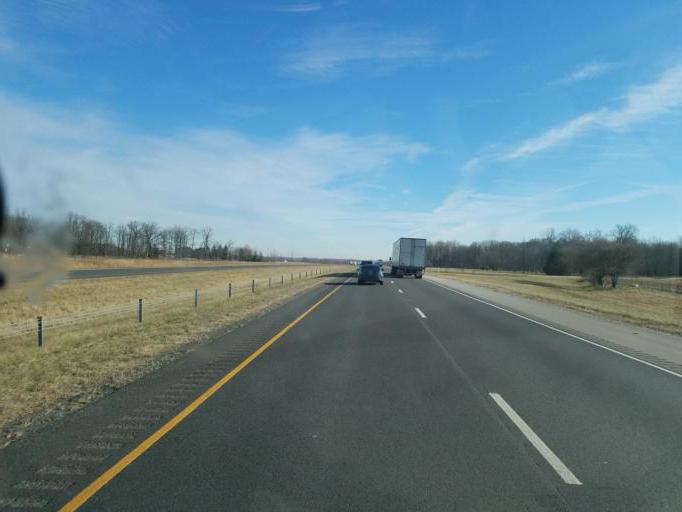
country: US
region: Indiana
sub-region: Wayne County
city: Centerville
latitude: 39.8596
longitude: -85.0269
